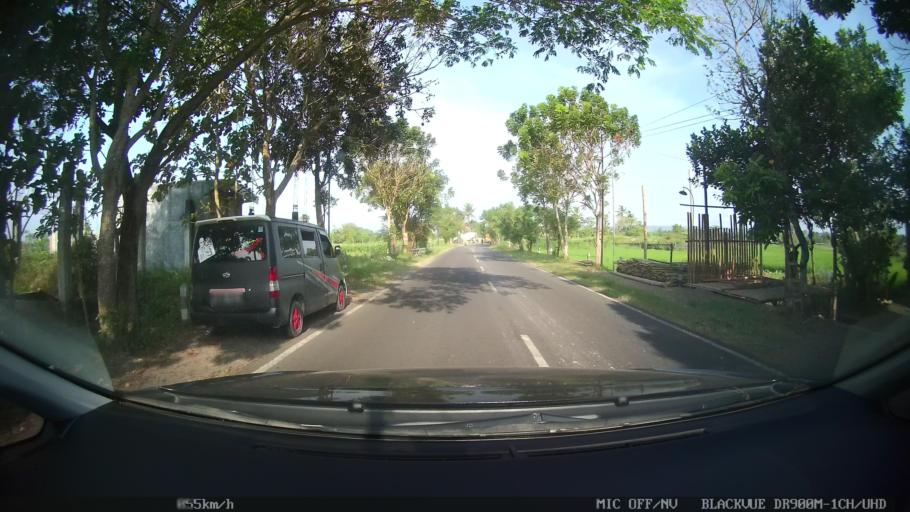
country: ID
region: Daerah Istimewa Yogyakarta
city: Pandak
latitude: -7.9021
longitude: 110.3046
